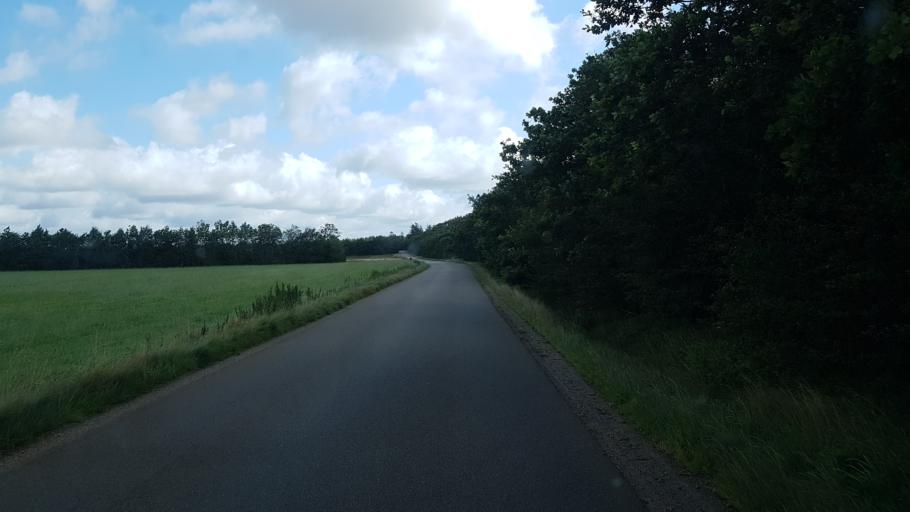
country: DK
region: South Denmark
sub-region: Varde Kommune
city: Olgod
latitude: 55.7871
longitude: 8.7312
